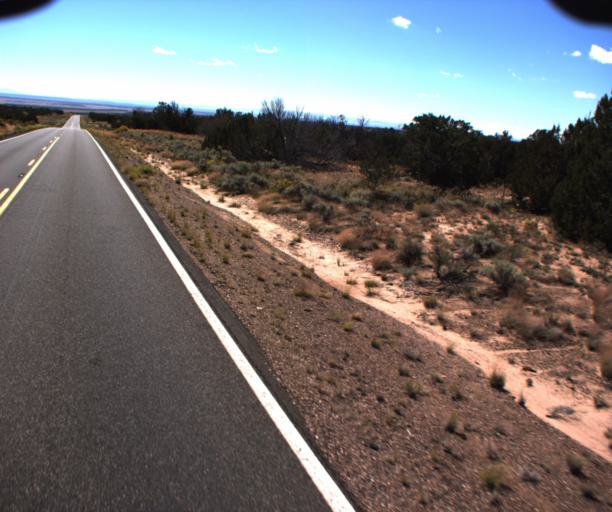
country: US
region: Arizona
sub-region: Apache County
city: Saint Johns
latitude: 34.8297
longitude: -109.2375
